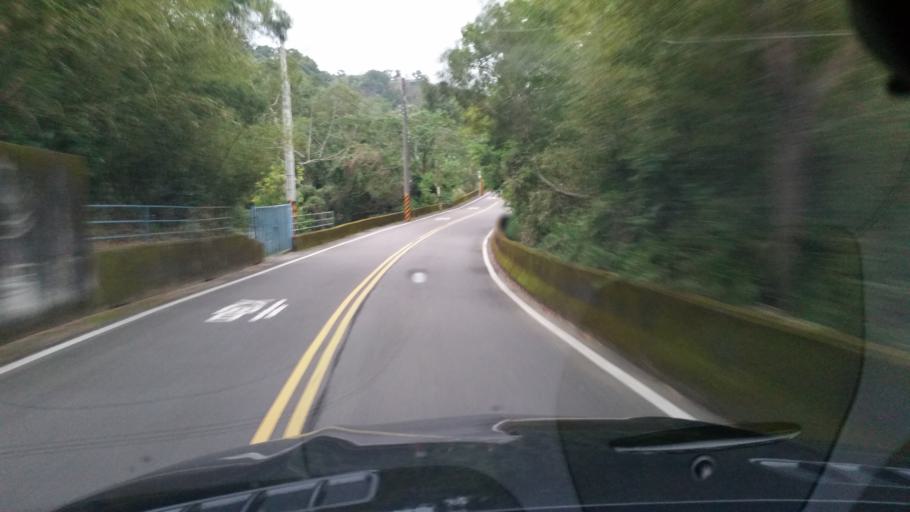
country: TW
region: Taiwan
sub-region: Miaoli
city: Miaoli
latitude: 24.5837
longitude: 120.8907
